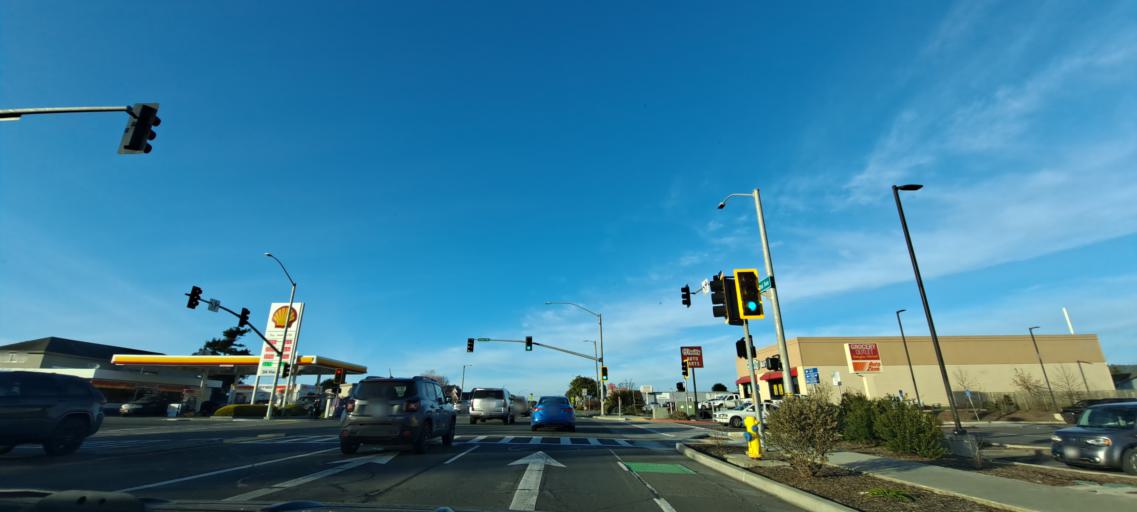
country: US
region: California
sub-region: Humboldt County
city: McKinleyville
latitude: 40.9339
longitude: -124.1008
